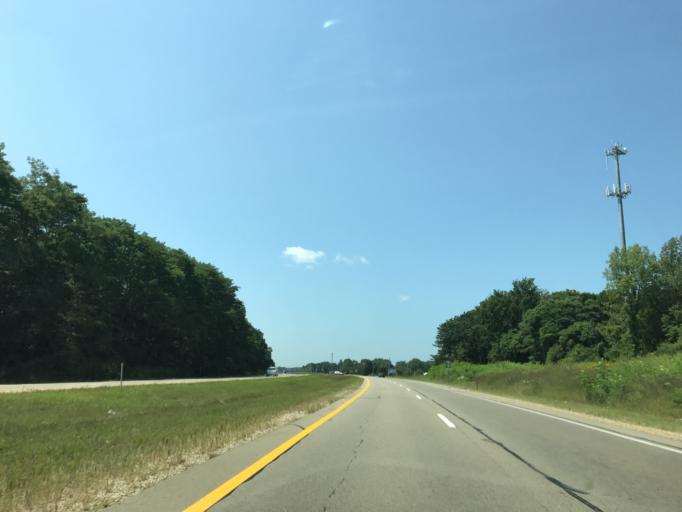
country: US
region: Michigan
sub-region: Berrien County
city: Niles
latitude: 41.8050
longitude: -86.2946
